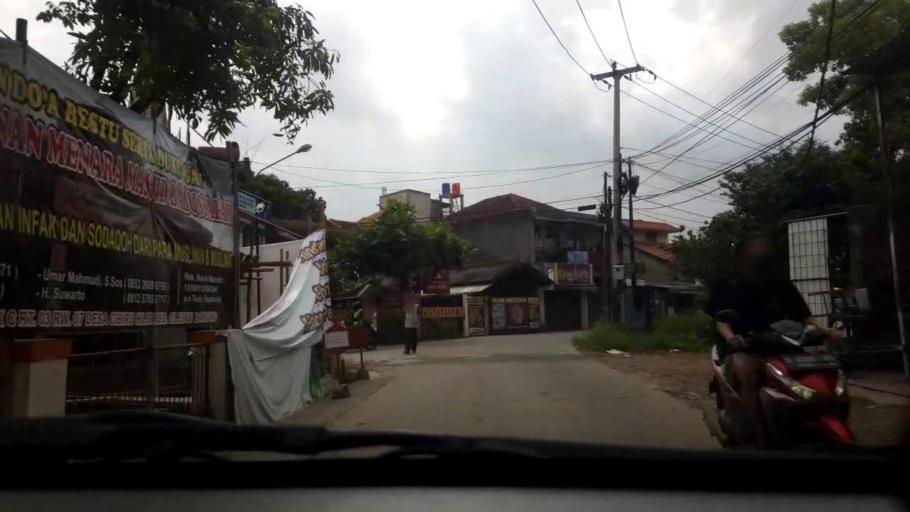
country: ID
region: West Java
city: Cileunyi
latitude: -6.9432
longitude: 107.7218
